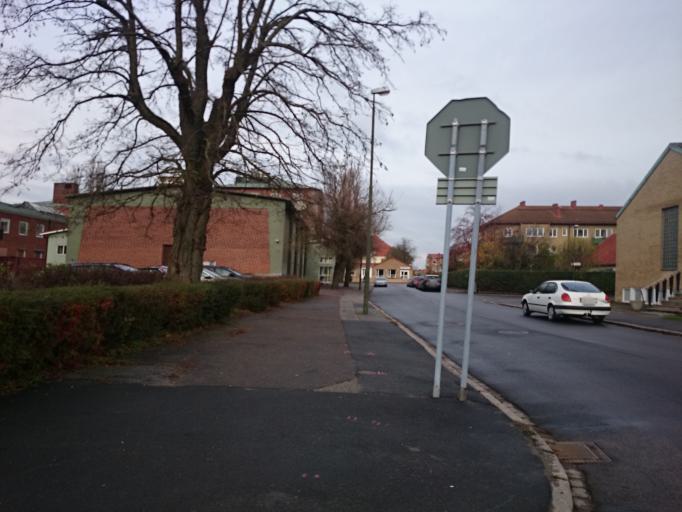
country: SE
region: Skane
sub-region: Malmo
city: Bunkeflostrand
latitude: 55.5803
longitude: 12.9374
